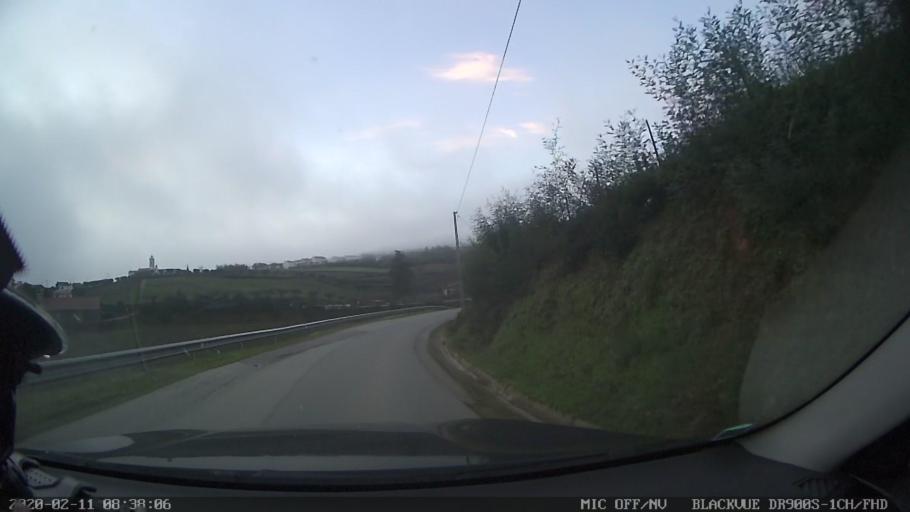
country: PT
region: Vila Real
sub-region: Sabrosa
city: Sabrosa
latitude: 41.2507
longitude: -7.5851
